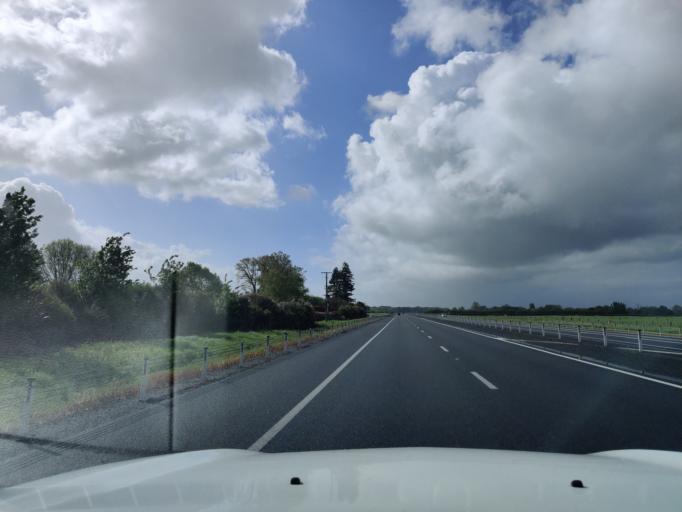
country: NZ
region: Waikato
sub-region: Waipa District
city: Cambridge
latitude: -37.8497
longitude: 175.3855
